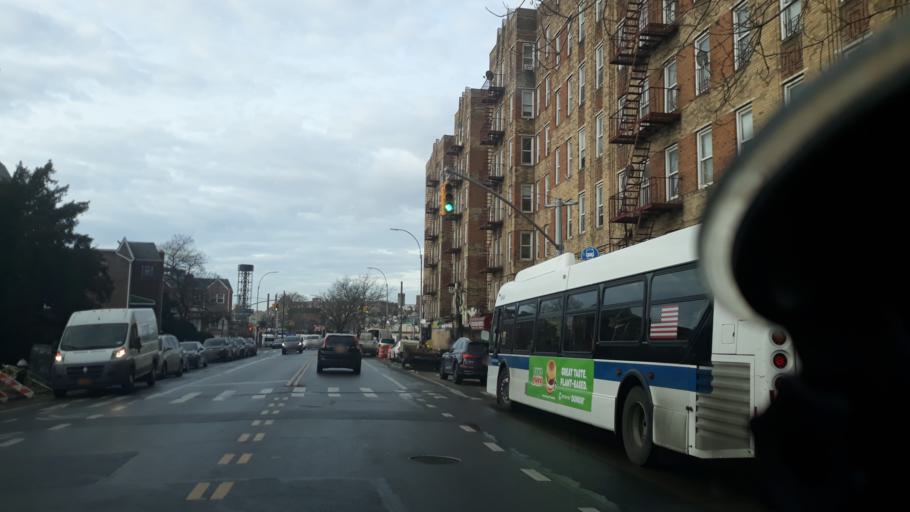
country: US
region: New York
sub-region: Kings County
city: Brooklyn
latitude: 40.6641
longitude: -73.9298
